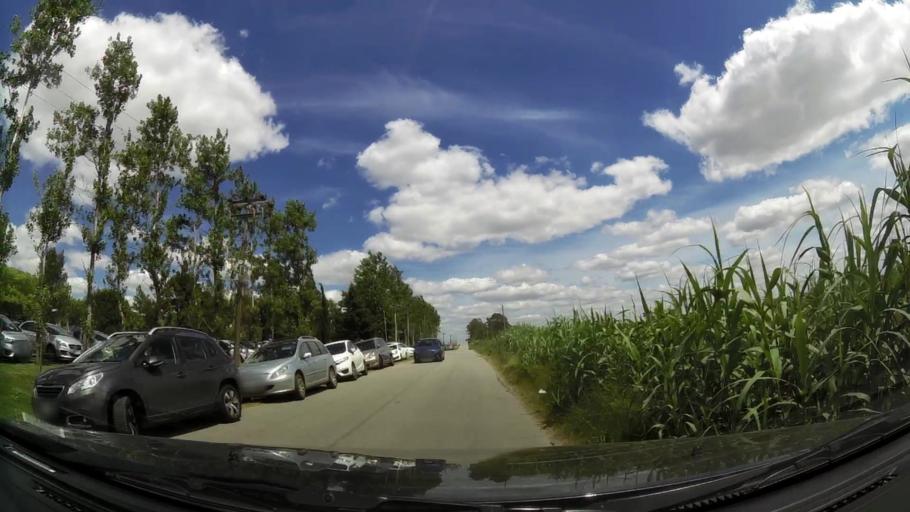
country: UY
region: Canelones
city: Colonia Nicolich
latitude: -34.8003
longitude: -56.0051
